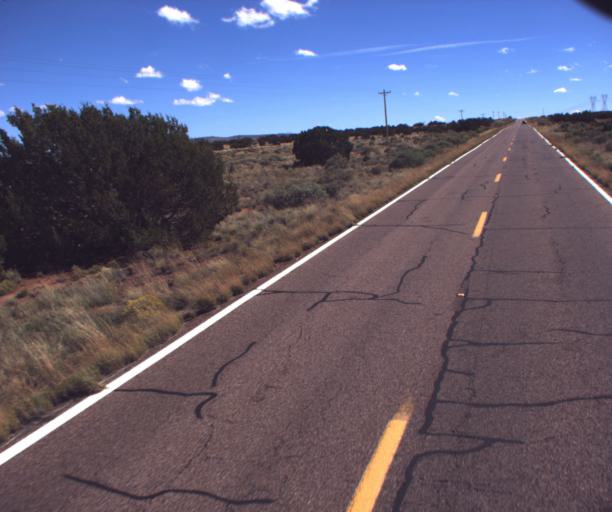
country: US
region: Arizona
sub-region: Apache County
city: Saint Johns
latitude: 34.5654
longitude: -109.6317
